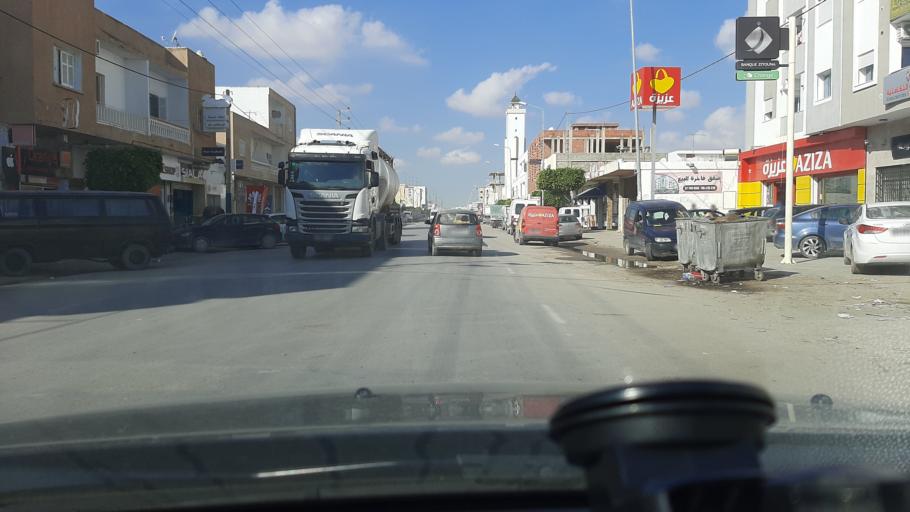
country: TN
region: Safaqis
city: Sfax
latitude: 34.7922
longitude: 10.7162
